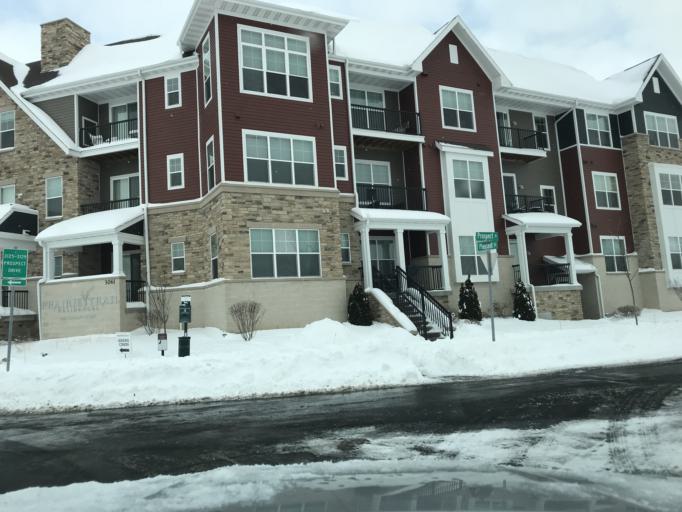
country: US
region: Wisconsin
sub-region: Dane County
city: Sun Prairie
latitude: 43.1670
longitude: -89.2792
